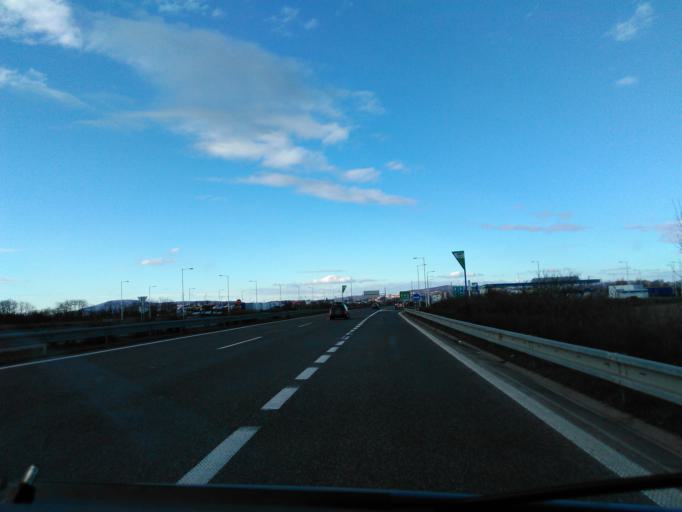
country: AT
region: Burgenland
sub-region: Politischer Bezirk Neusiedl am See
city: Kittsee
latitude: 48.0842
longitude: 17.0996
